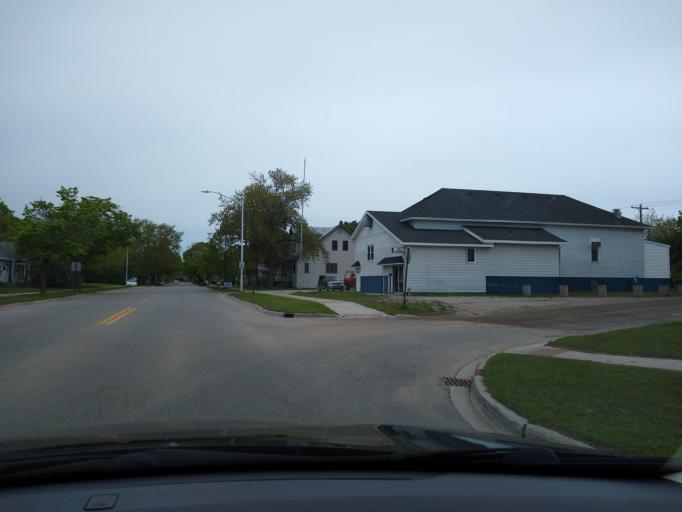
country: US
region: Michigan
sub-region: Delta County
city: Escanaba
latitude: 45.7561
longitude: -87.0714
